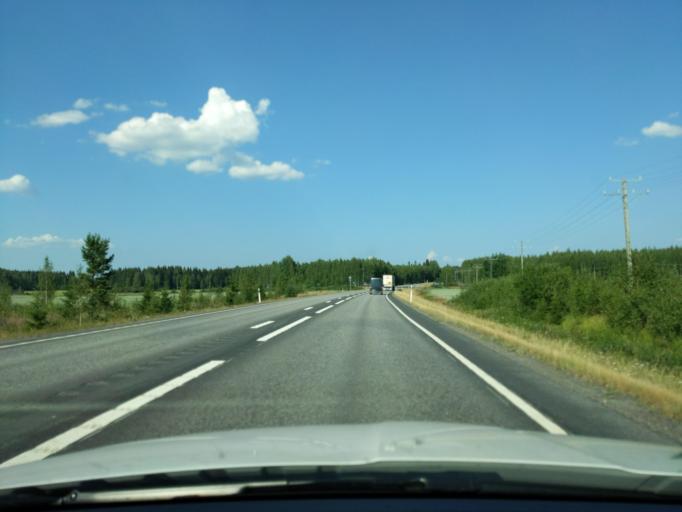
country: FI
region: Paijanne Tavastia
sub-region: Lahti
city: Jaervelae
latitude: 60.9218
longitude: 25.3606
